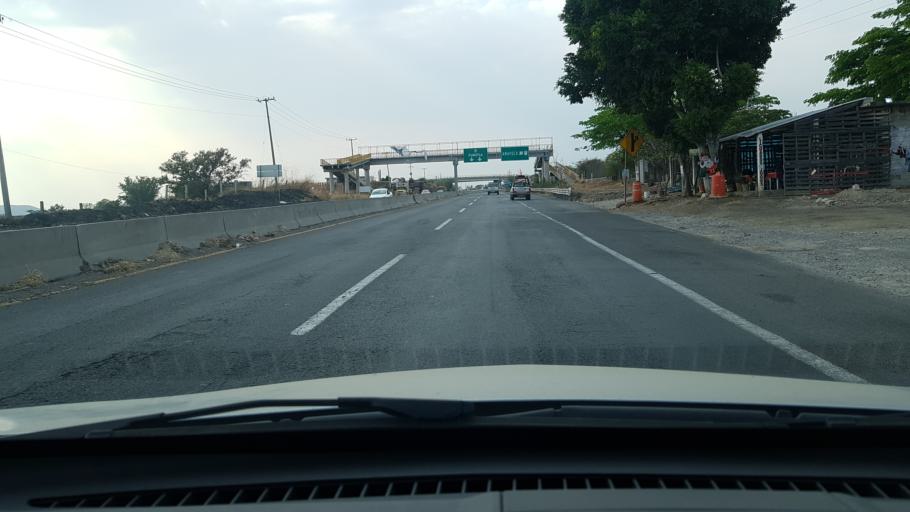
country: MX
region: Morelos
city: Amayuca
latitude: 18.7279
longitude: -98.8092
